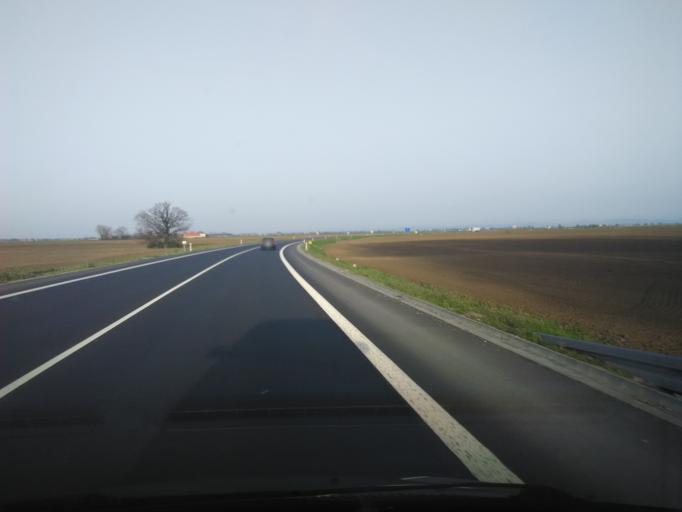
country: SK
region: Trnavsky
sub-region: Okres Galanta
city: Galanta
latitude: 48.1770
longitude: 17.7155
